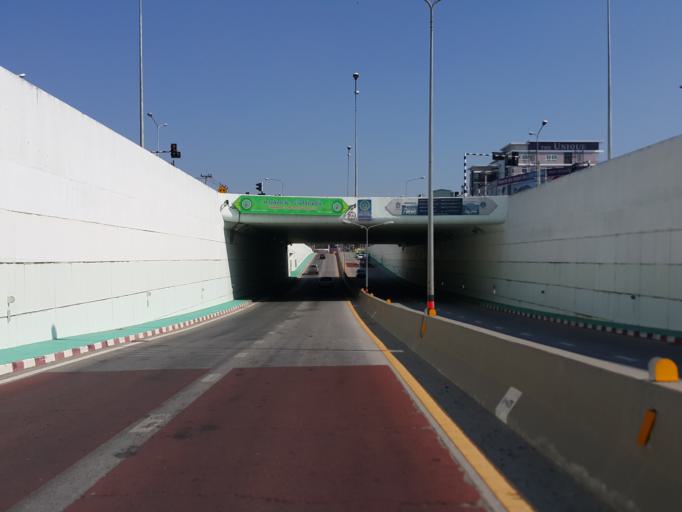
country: TH
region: Chiang Mai
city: San Sai
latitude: 18.8232
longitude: 99.0110
